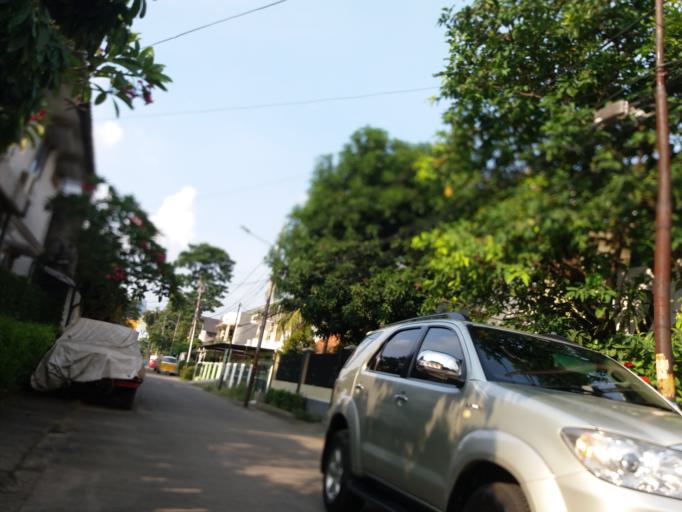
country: ID
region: Jakarta Raya
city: Jakarta
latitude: -6.2479
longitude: 106.8100
